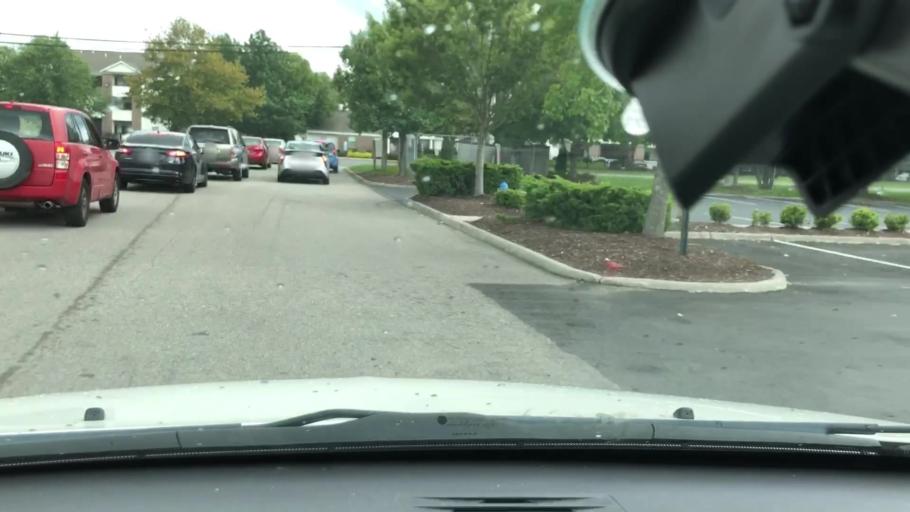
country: US
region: Virginia
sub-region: City of Chesapeake
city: Chesapeake
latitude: 36.7875
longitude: -76.2658
